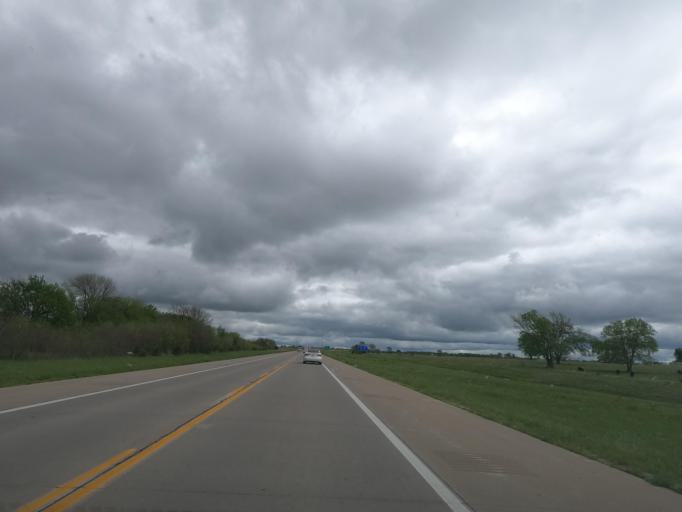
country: US
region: Kansas
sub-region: Montgomery County
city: Cherryvale
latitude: 37.3469
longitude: -95.5448
